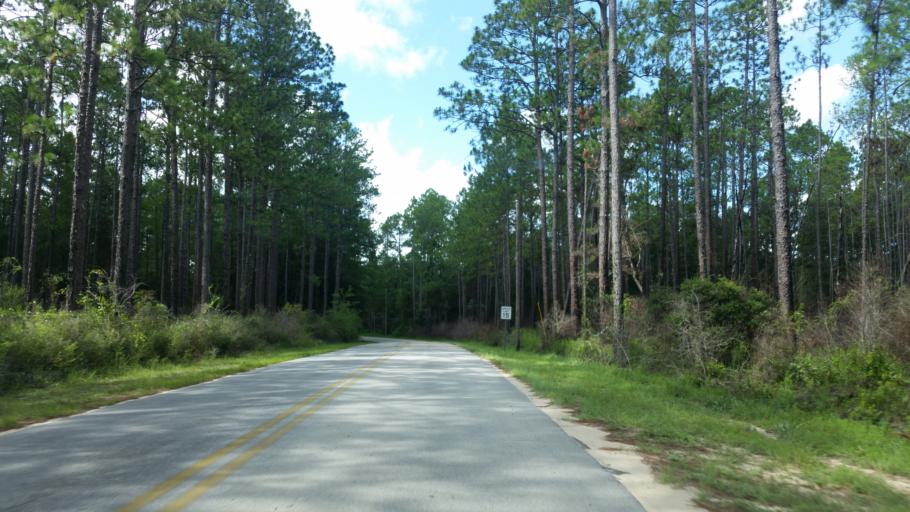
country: US
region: Florida
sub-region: Santa Rosa County
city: East Milton
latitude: 30.7084
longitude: -86.8825
